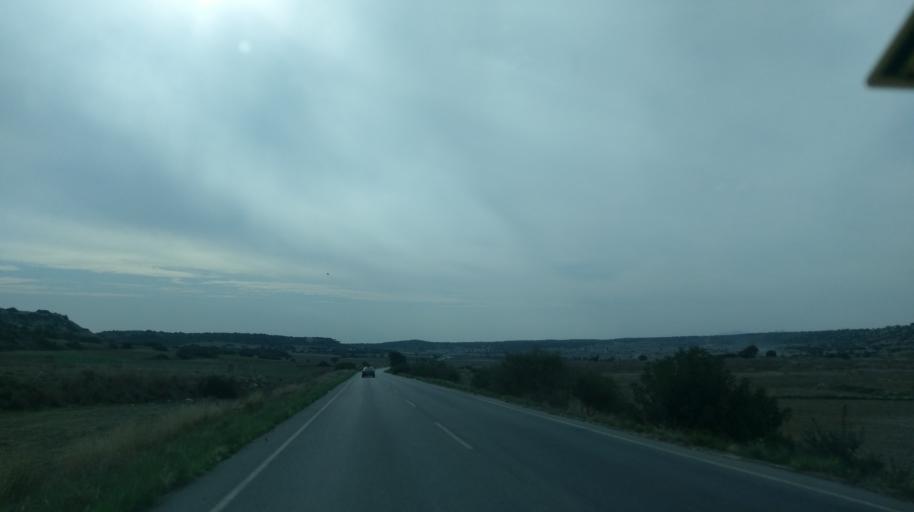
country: CY
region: Ammochostos
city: Leonarisso
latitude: 35.4653
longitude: 34.1400
